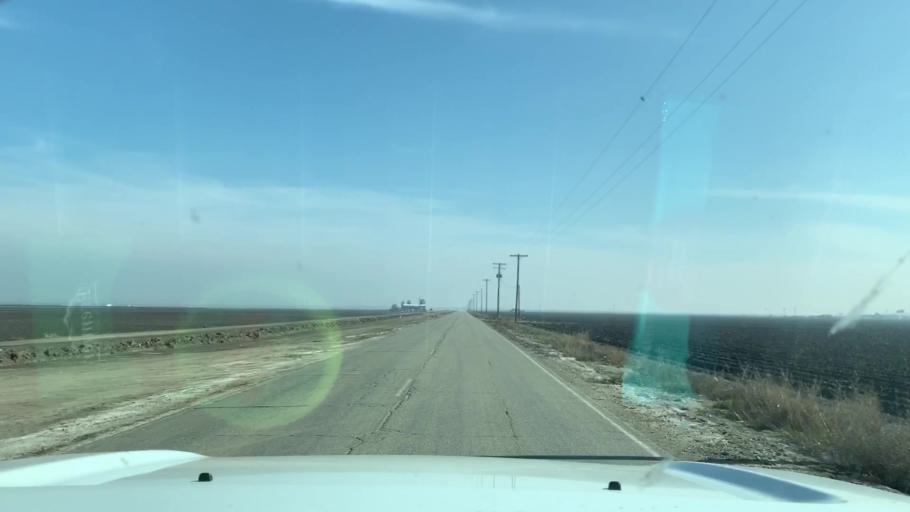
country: US
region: California
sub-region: Kern County
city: Buttonwillow
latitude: 35.4420
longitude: -119.5281
